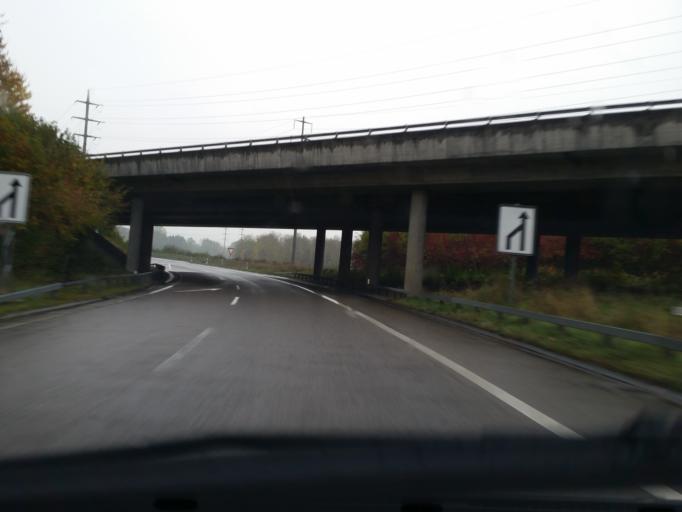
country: CH
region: Thurgau
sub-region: Frauenfeld District
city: Mullheim
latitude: 47.5901
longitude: 8.9984
